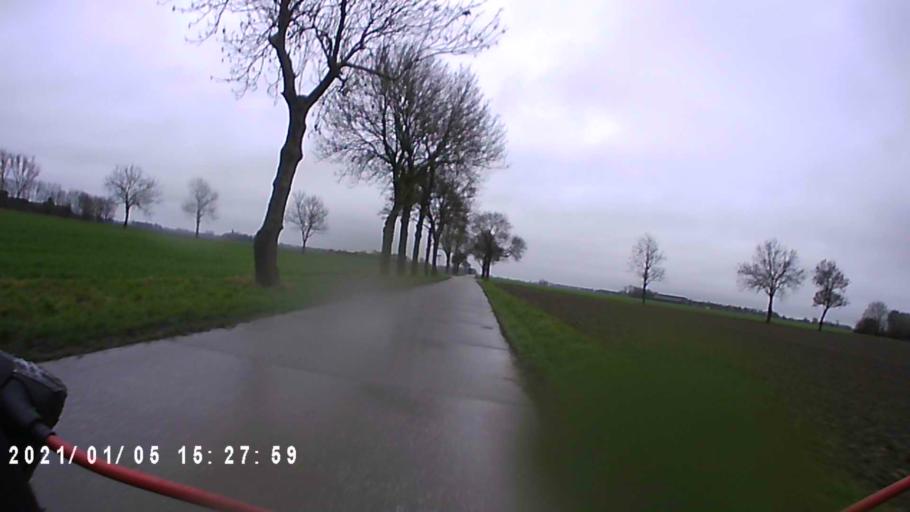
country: DE
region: Lower Saxony
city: Bunde
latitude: 53.2177
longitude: 7.1953
